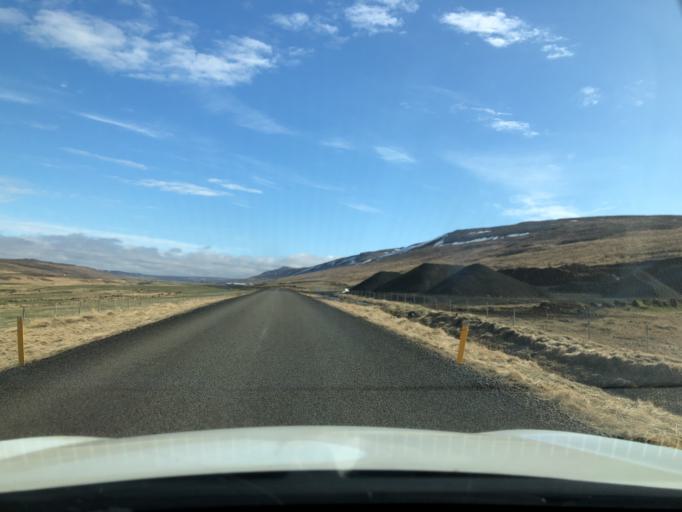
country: IS
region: West
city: Borgarnes
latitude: 65.1309
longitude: -21.6186
